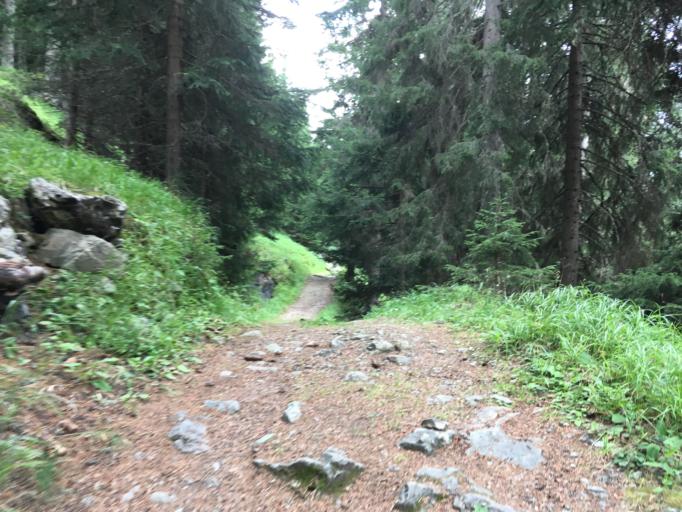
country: CH
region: Grisons
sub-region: Maloja District
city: Silvaplana
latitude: 46.4810
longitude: 9.6486
